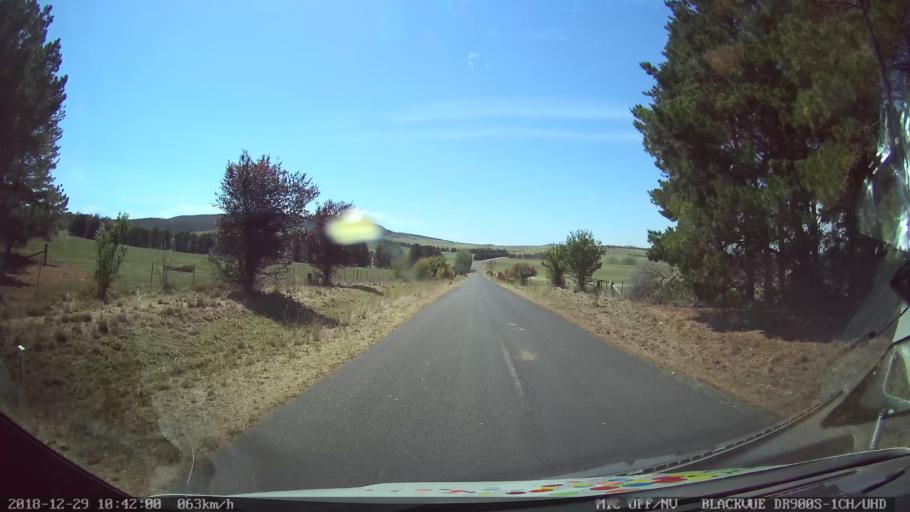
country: AU
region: New South Wales
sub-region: Palerang
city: Bungendore
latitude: -35.0297
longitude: 149.5255
